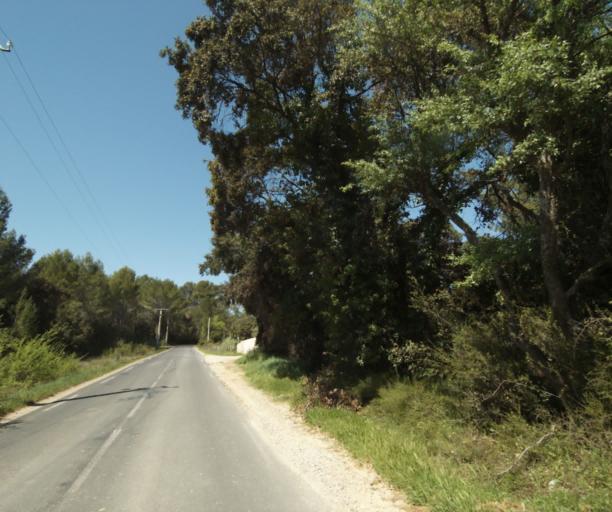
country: FR
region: Languedoc-Roussillon
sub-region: Departement de l'Herault
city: Saint-Genies-des-Mourgues
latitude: 43.6885
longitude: 4.0178
